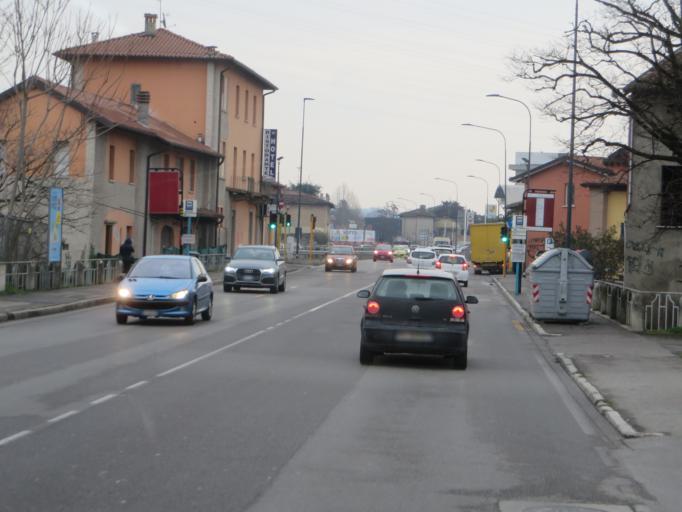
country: IT
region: Lombardy
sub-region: Provincia di Brescia
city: Buffalora-Bettole
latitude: 45.5205
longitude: 10.2737
